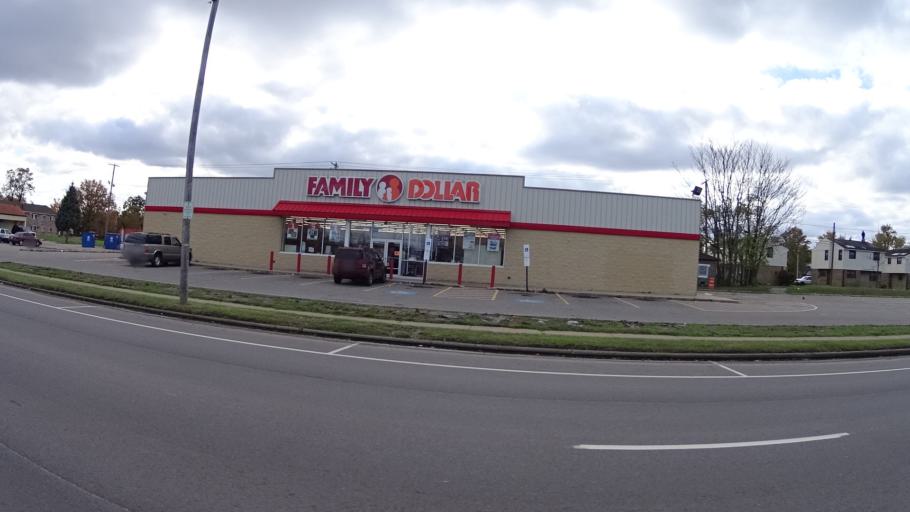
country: US
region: Ohio
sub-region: Lorain County
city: Lorain
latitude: 41.4453
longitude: -82.1463
